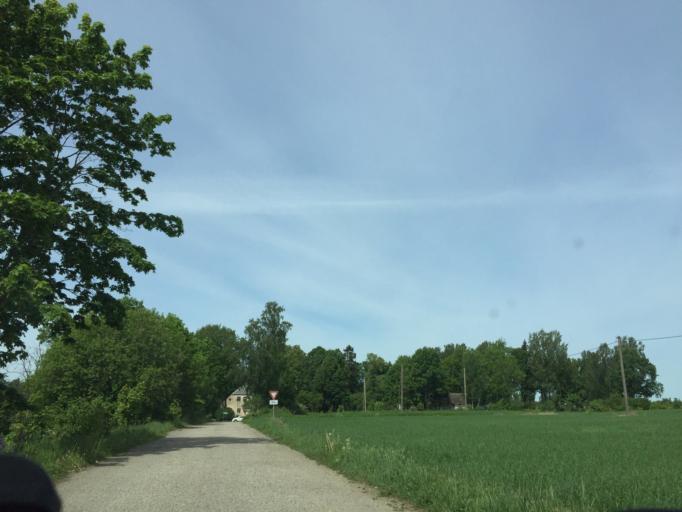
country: LV
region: Koceni
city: Koceni
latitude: 57.4652
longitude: 25.2665
